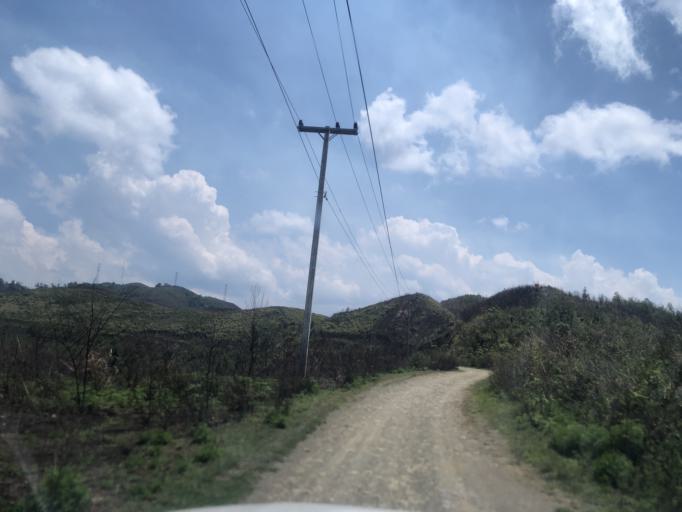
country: LA
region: Phongsali
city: Phongsali
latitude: 21.4067
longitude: 102.1862
